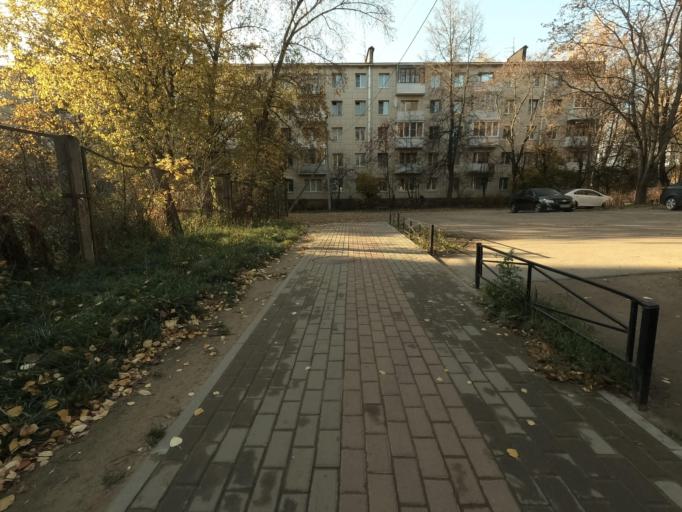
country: RU
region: Leningrad
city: Sertolovo
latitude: 60.1500
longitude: 30.2069
